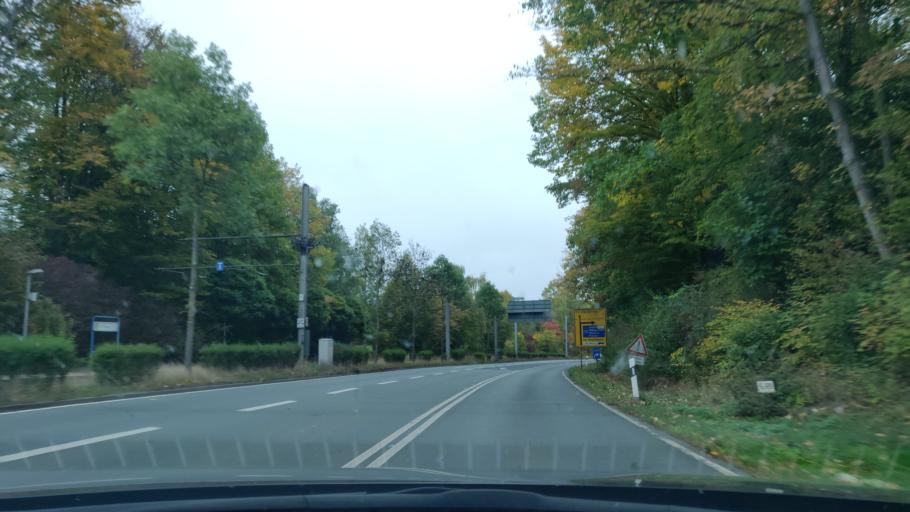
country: DE
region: Hesse
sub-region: Regierungsbezirk Kassel
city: Baunatal
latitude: 51.2639
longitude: 9.4255
